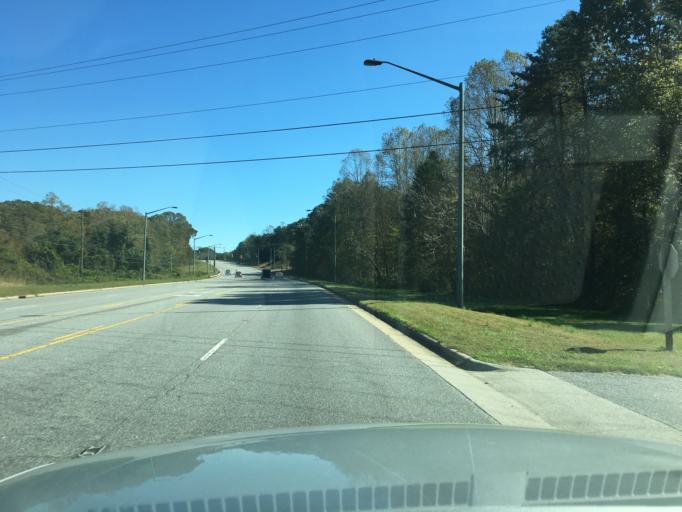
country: US
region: North Carolina
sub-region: Catawba County
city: Saint Stephens
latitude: 35.7181
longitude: -81.2728
